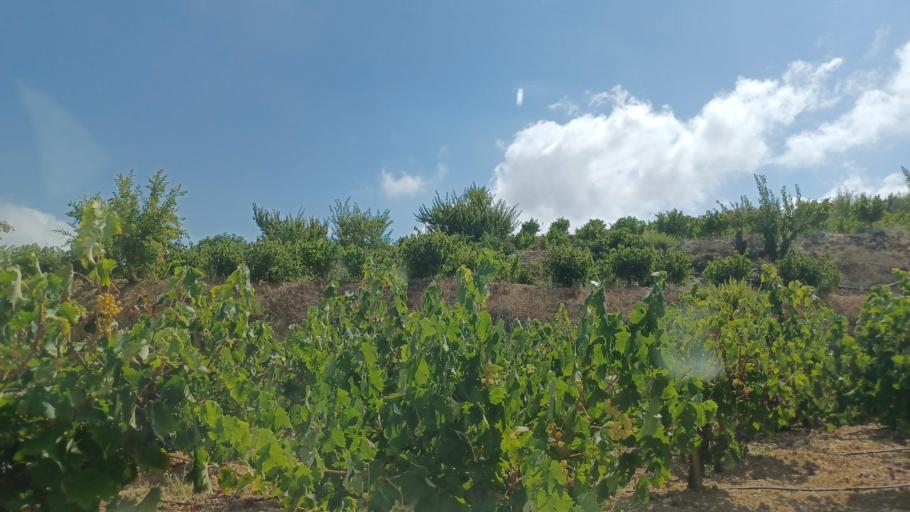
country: CY
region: Pafos
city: Tala
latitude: 34.8707
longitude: 32.4543
